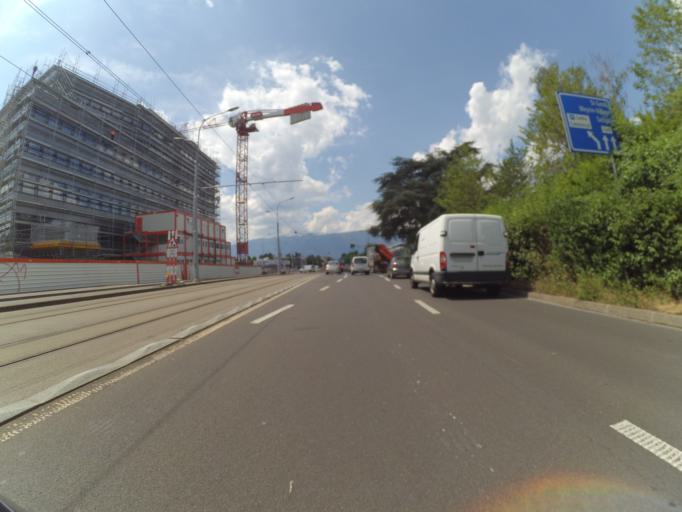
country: CH
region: Geneva
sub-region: Geneva
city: Meyrin
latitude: 46.2268
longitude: 6.0797
